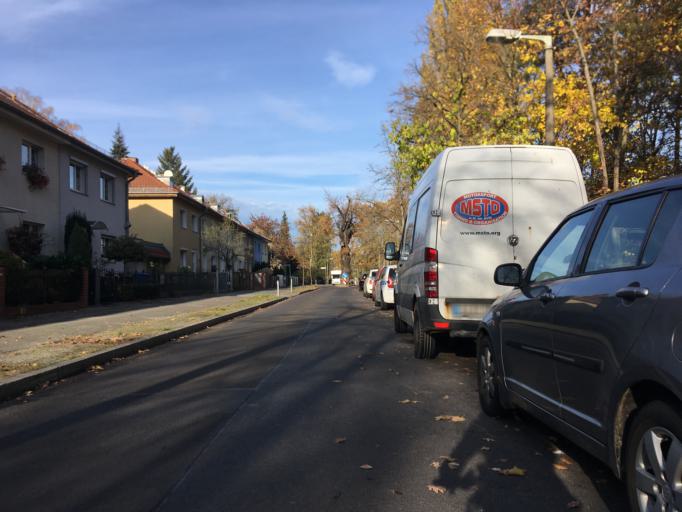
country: DE
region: Berlin
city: Karlshorst
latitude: 52.4891
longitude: 13.5330
